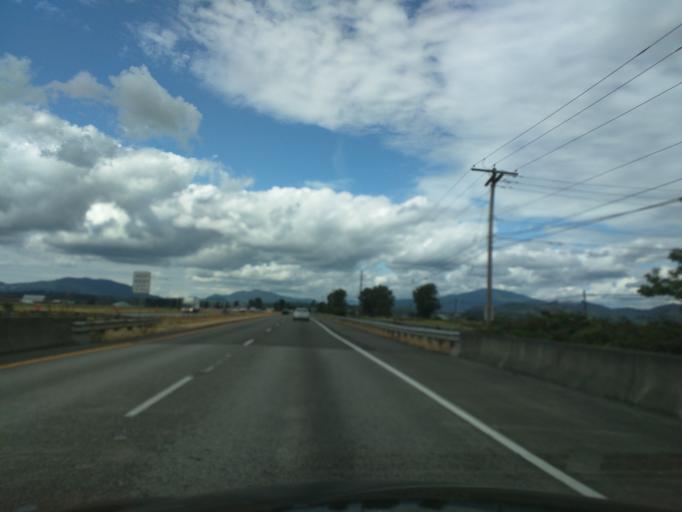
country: US
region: Washington
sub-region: Skagit County
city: Burlington
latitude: 48.4932
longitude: -122.3353
